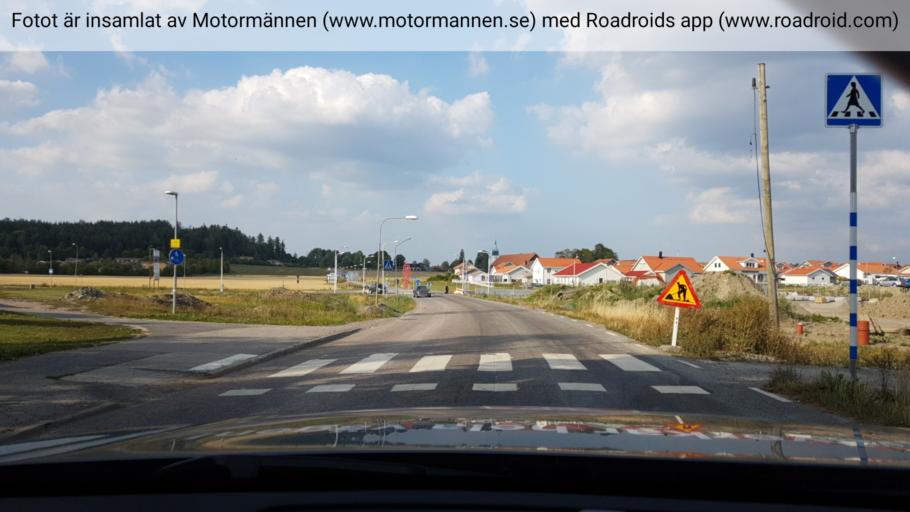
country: SE
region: Soedermanland
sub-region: Gnesta Kommun
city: Gnesta
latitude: 59.0523
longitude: 17.3027
